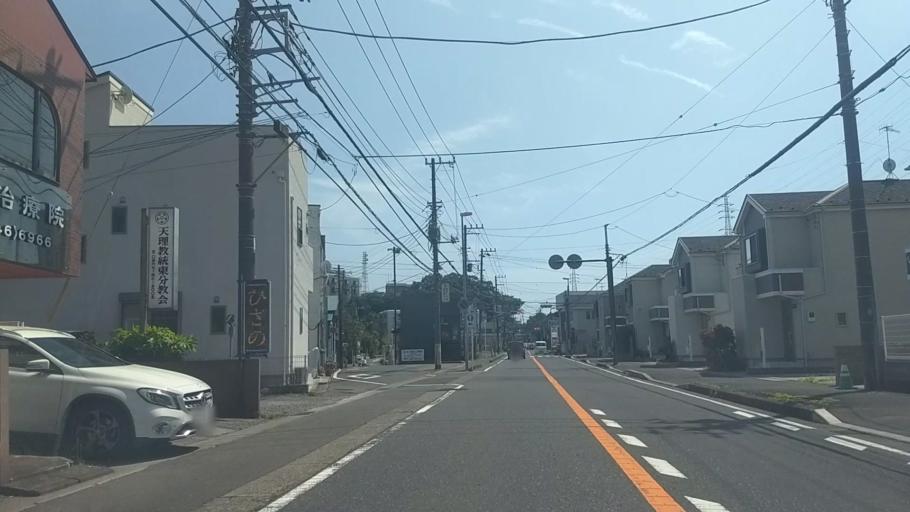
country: JP
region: Kanagawa
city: Kamakura
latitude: 35.3554
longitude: 139.5450
